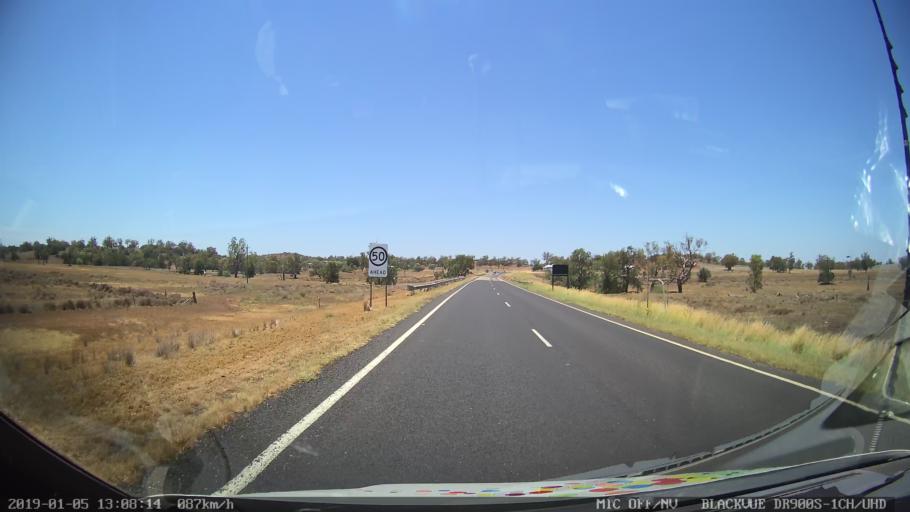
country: AU
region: New South Wales
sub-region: Gunnedah
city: Gunnedah
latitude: -31.0988
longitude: 149.8991
